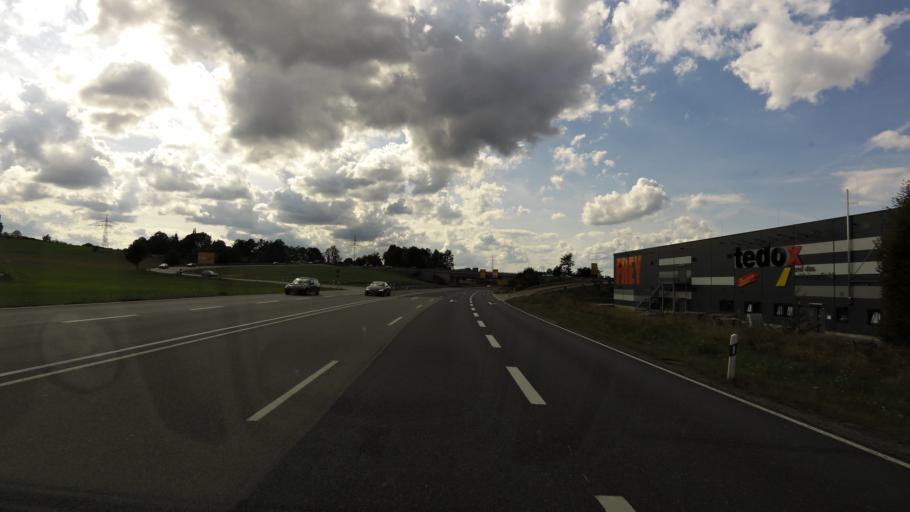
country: DE
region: Bavaria
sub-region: Upper Palatinate
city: Cham
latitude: 49.2003
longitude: 12.6629
